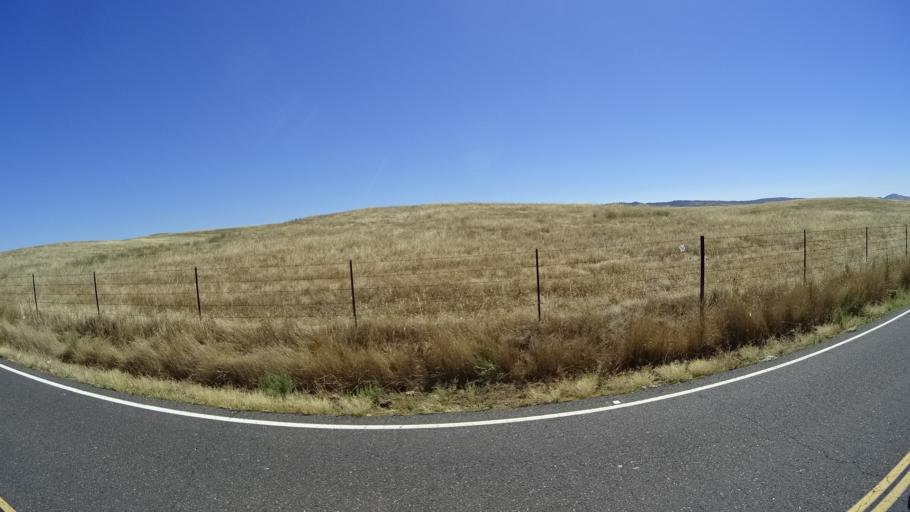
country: US
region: California
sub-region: Calaveras County
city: Rancho Calaveras
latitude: 38.0188
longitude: -120.8538
